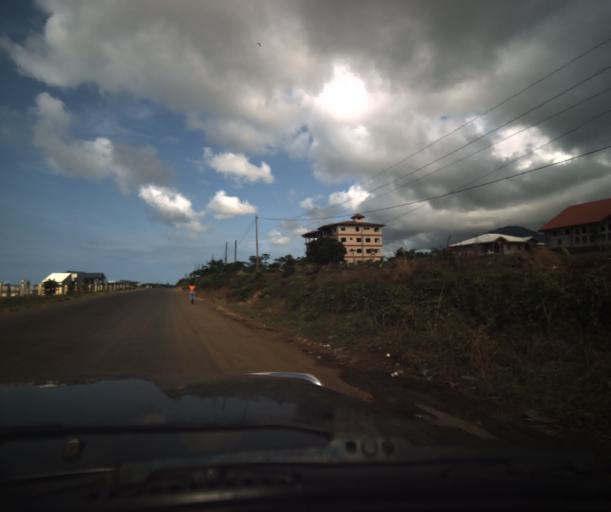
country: CM
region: South-West Province
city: Limbe
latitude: 4.0159
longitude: 9.1659
